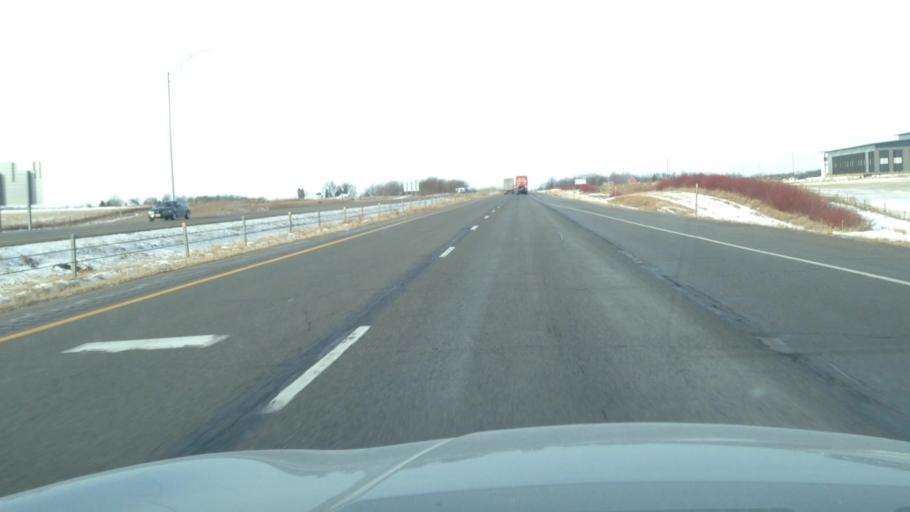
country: US
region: Iowa
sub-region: Poweshiek County
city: Grinnell
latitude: 41.6961
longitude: -92.7334
